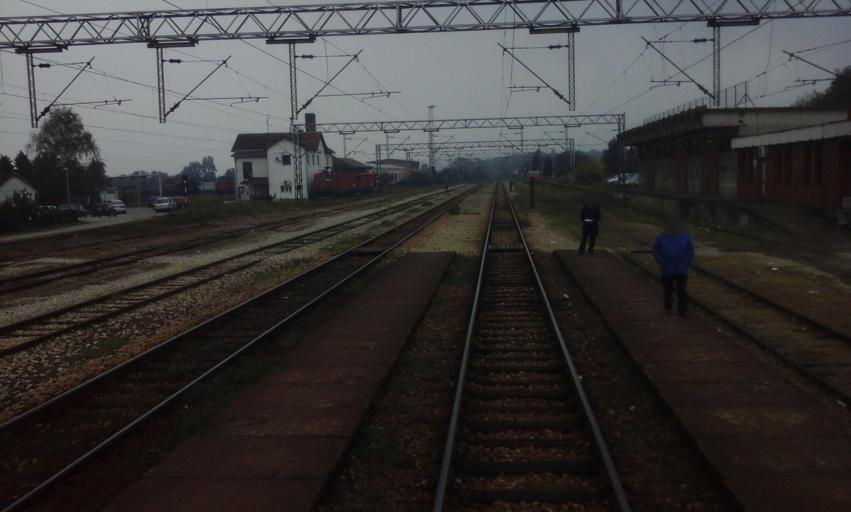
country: RS
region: Central Serbia
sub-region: Sumadijski Okrug
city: Batocina
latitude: 44.1576
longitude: 21.1023
